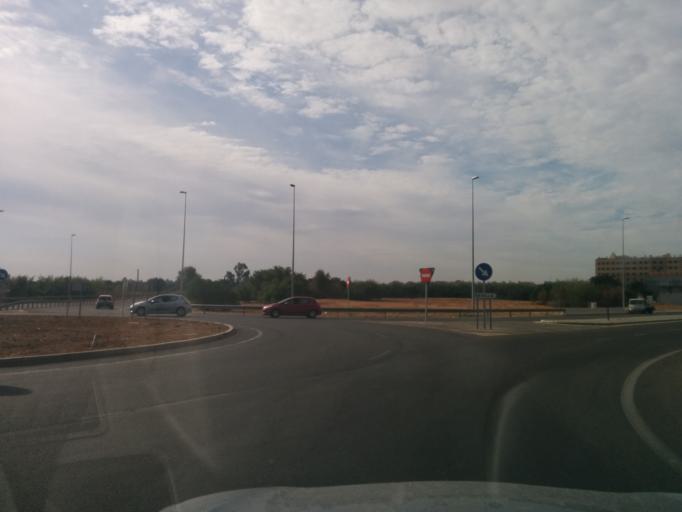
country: ES
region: Andalusia
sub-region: Provincia de Sevilla
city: Sevilla
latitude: 37.4341
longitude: -5.9666
